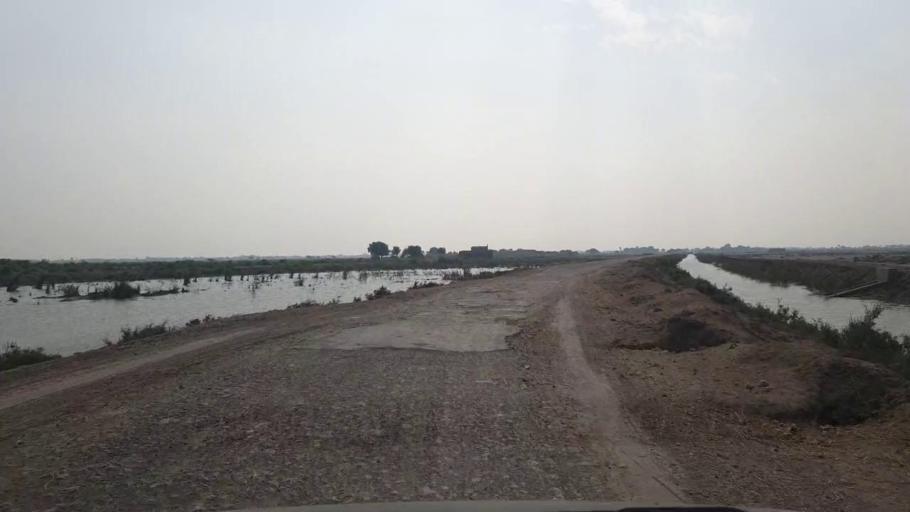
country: PK
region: Sindh
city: Tando Muhammad Khan
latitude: 25.0837
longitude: 68.3878
